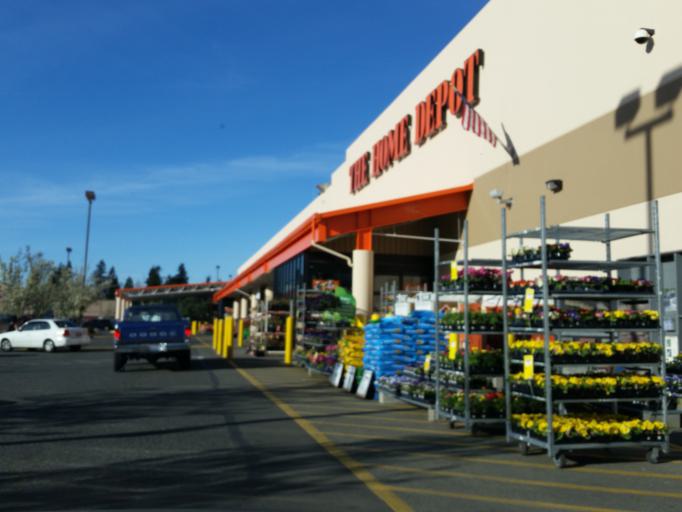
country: US
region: Washington
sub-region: Snohomish County
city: Esperance
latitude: 47.7755
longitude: -122.3427
